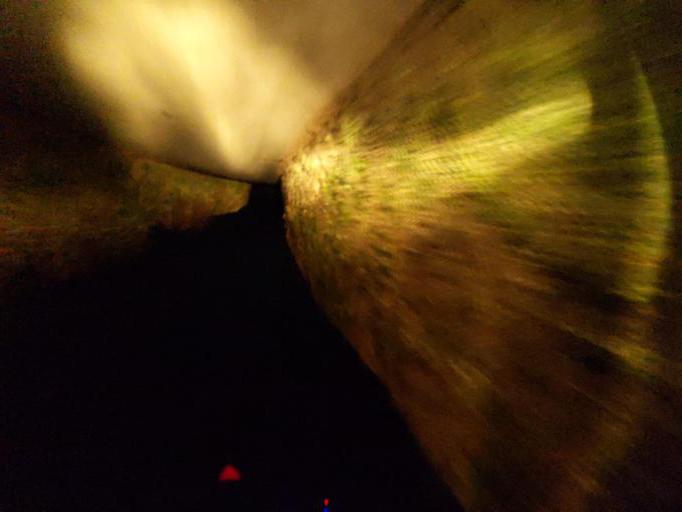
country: GB
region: England
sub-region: Cornwall
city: Torpoint
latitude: 50.3490
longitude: -4.2277
